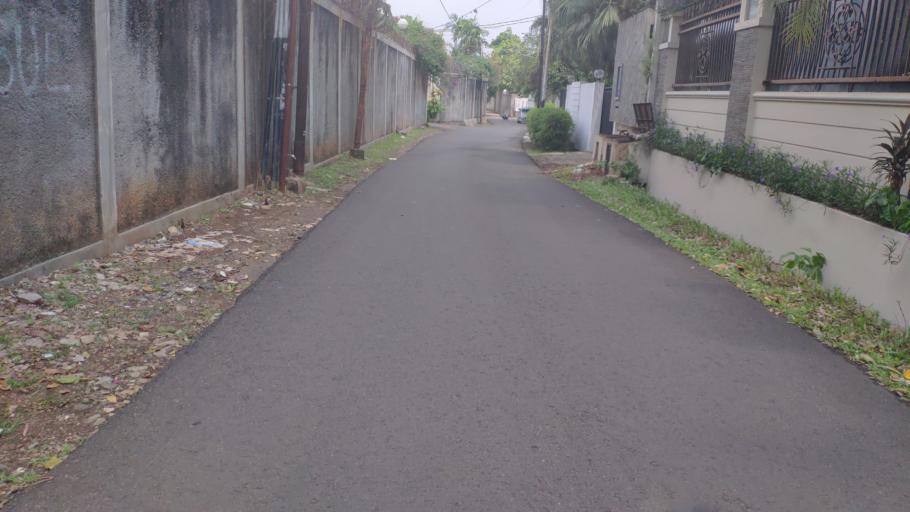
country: ID
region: Jakarta Raya
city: Jakarta
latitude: -6.2744
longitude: 106.8237
